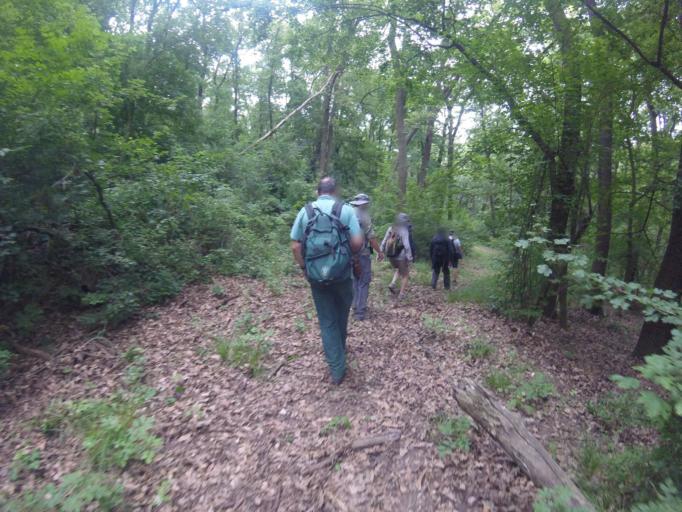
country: HU
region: Komarom-Esztergom
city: Labatlan
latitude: 47.6977
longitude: 18.4964
